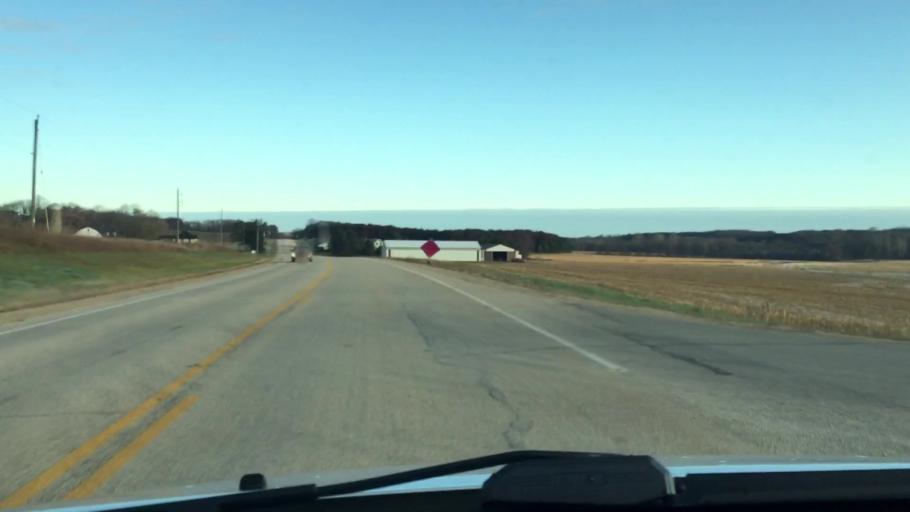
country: US
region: Wisconsin
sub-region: Washington County
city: Hartford
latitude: 43.2684
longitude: -88.4637
